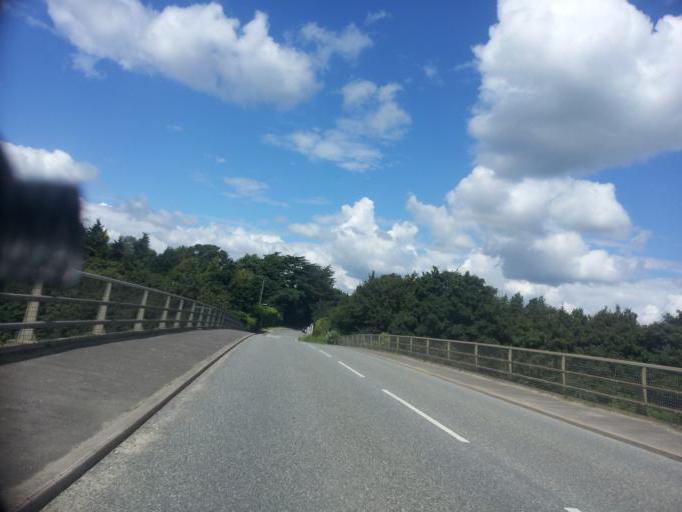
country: GB
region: England
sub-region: Kent
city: West Malling
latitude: 51.3089
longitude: 0.3902
